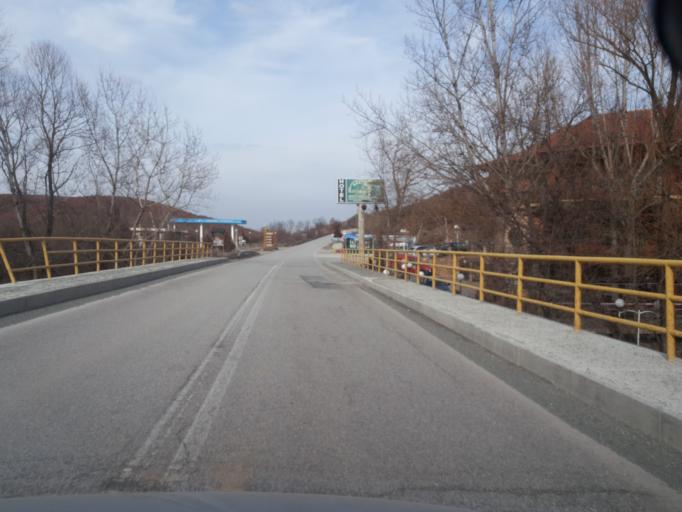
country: XK
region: Pec
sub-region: Komuna e Klines
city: Klina
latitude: 42.5236
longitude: 20.5615
